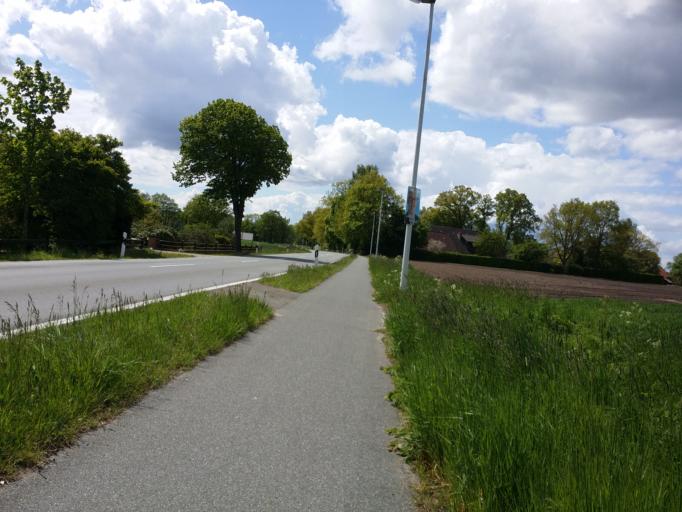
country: DE
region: Lower Saxony
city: Stuhr
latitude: 53.0055
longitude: 8.7239
